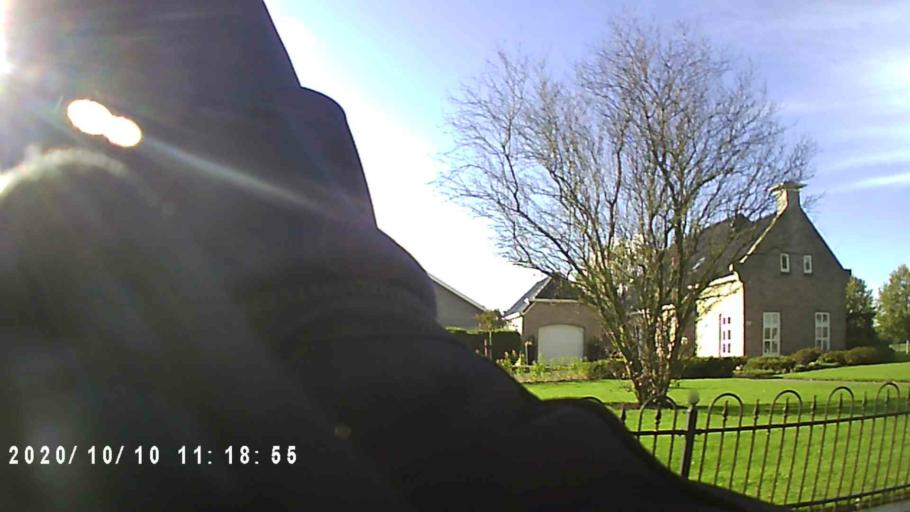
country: NL
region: Friesland
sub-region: Gemeente Smallingerland
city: Drachtstercompagnie
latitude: 53.0945
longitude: 6.1943
